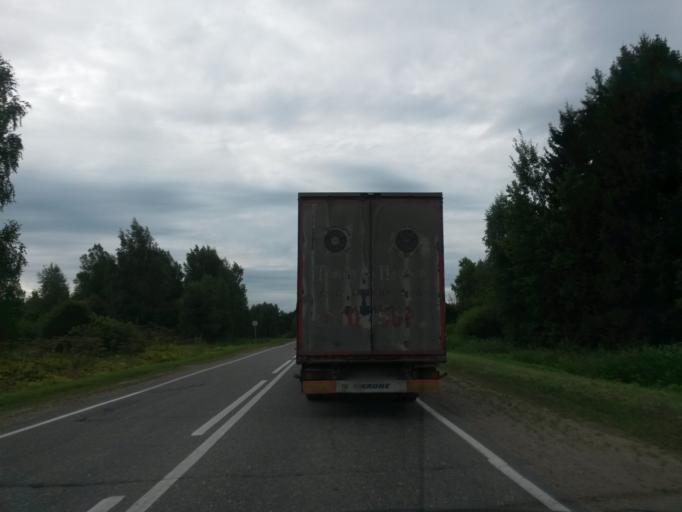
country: RU
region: Jaroslavl
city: Krasnyye Tkachi
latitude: 57.3673
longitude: 39.7366
